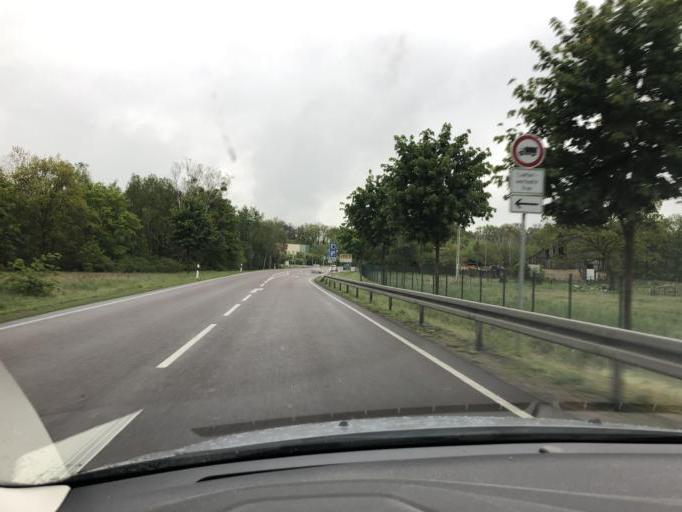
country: DE
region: Saxony-Anhalt
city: Dessau
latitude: 51.7905
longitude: 12.2348
